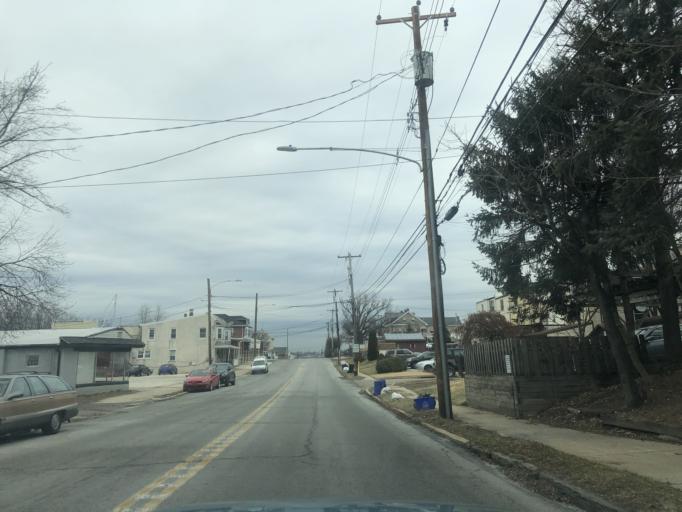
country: US
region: Pennsylvania
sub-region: Montgomery County
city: Bridgeport
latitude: 40.1011
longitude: -75.3496
